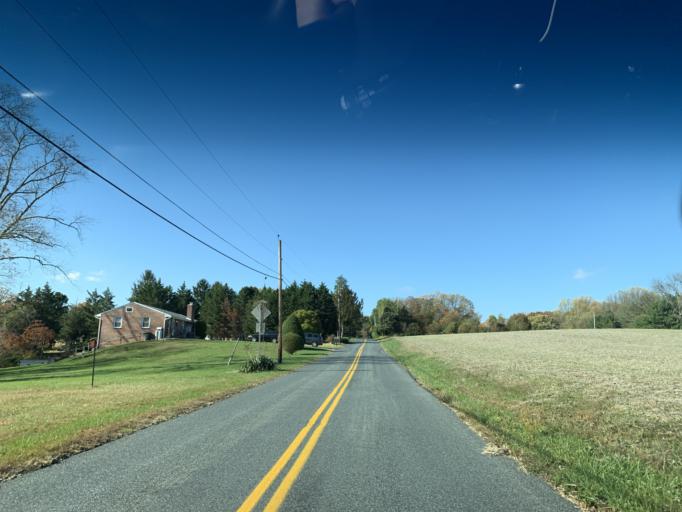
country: US
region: Maryland
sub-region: Harford County
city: Joppatowne
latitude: 39.4726
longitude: -76.3528
